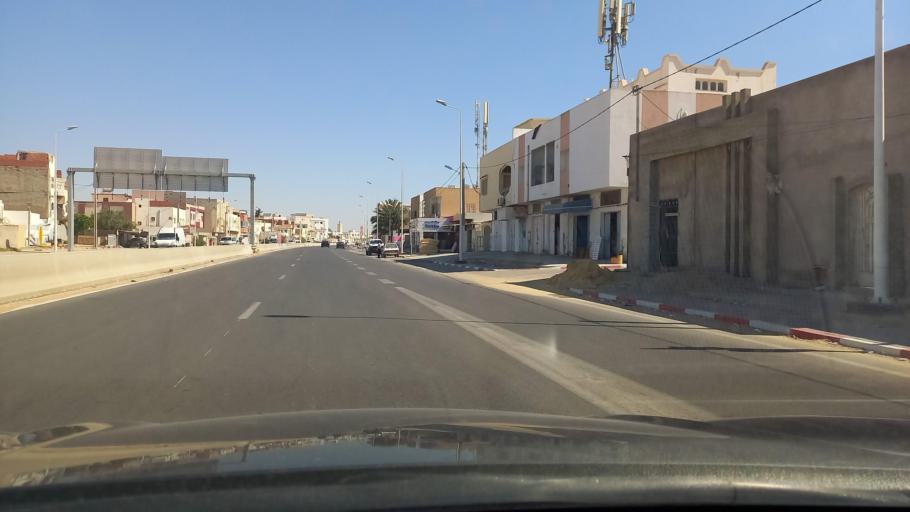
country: TN
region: Safaqis
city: Sfax
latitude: 34.7356
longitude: 10.7242
